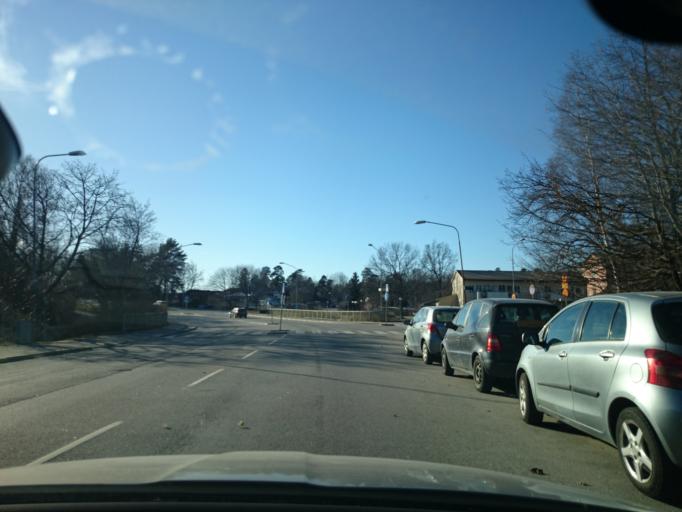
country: SE
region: Stockholm
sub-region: Stockholms Kommun
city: Arsta
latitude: 59.2434
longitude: 18.0836
